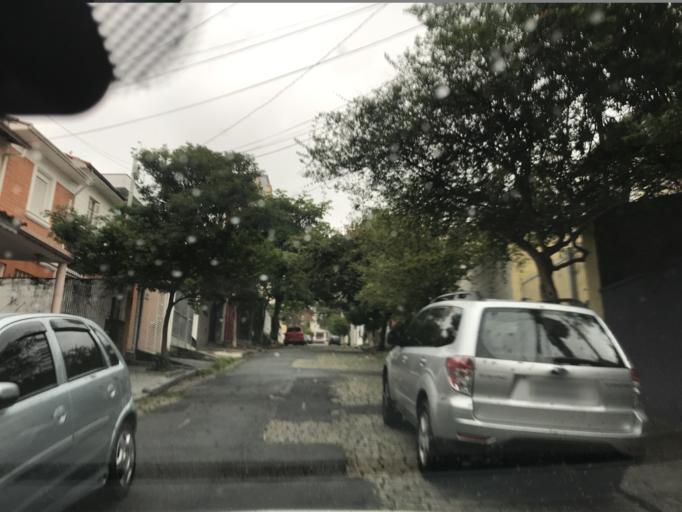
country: BR
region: Sao Paulo
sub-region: Sao Paulo
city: Sao Paulo
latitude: -23.5360
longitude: -46.6812
